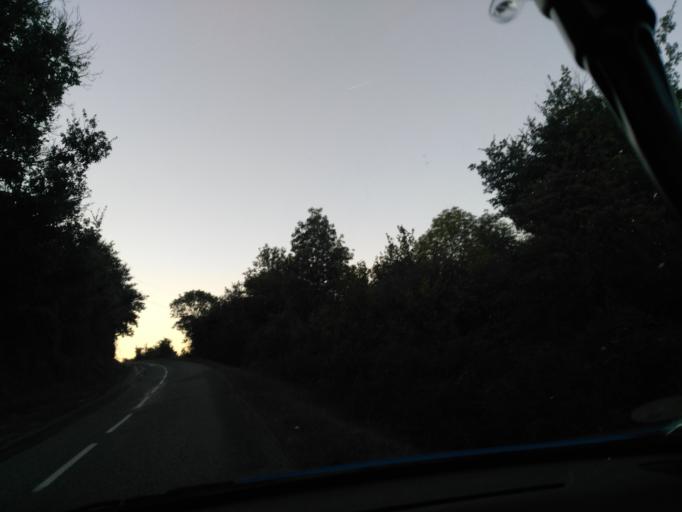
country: FR
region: Rhone-Alpes
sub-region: Departement du Rhone
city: Limonest
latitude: 45.8416
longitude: 4.7934
